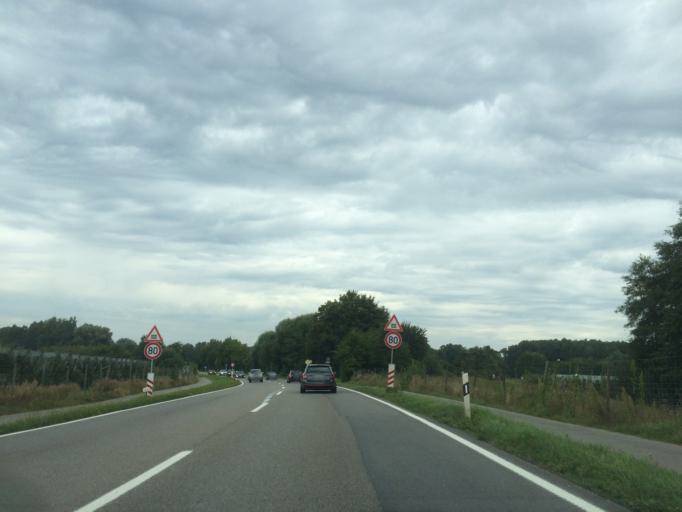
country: DE
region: Baden-Wuerttemberg
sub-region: Tuebingen Region
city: Immenstaad am Bodensee
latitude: 47.6716
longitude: 9.3975
